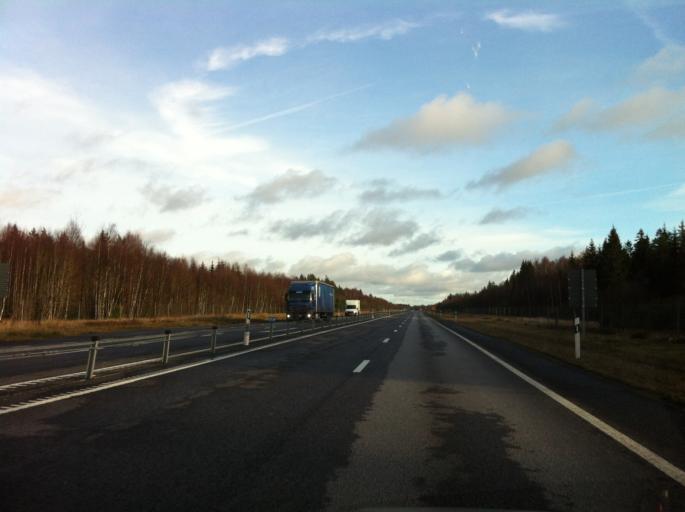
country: SE
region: Kronoberg
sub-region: Alvesta Kommun
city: Vislanda
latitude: 56.6671
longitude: 14.3068
